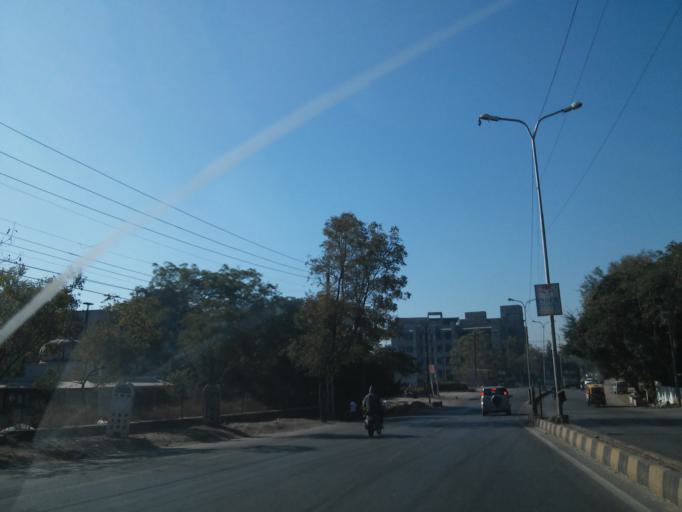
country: IN
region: Rajasthan
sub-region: Udaipur
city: Udaipur
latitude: 24.5540
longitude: 73.6914
